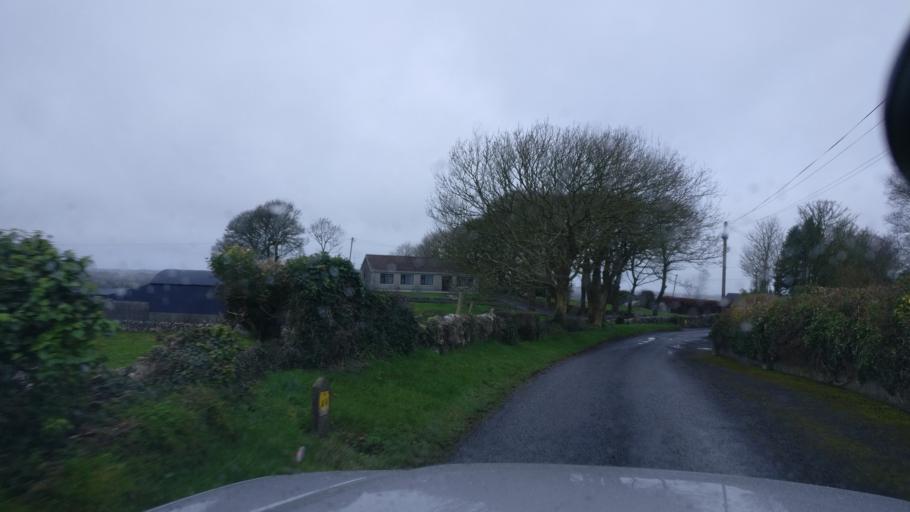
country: IE
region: Connaught
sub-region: County Galway
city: Loughrea
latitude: 53.1837
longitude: -8.6065
